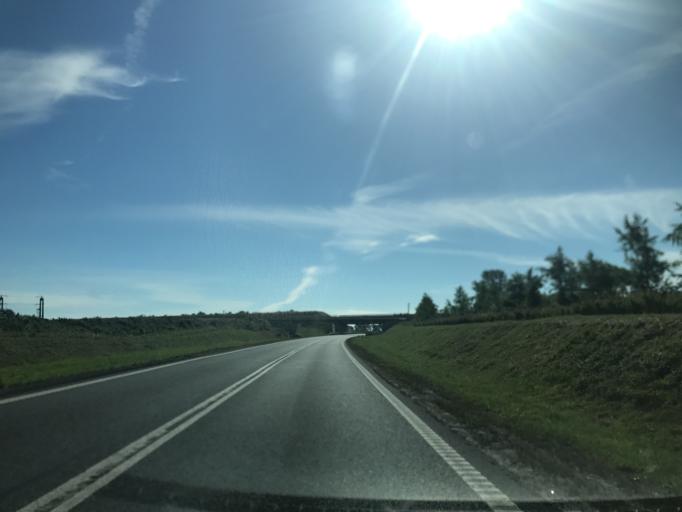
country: PL
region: Pomeranian Voivodeship
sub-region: Powiat chojnicki
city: Chojnice
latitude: 53.6806
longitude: 17.5628
